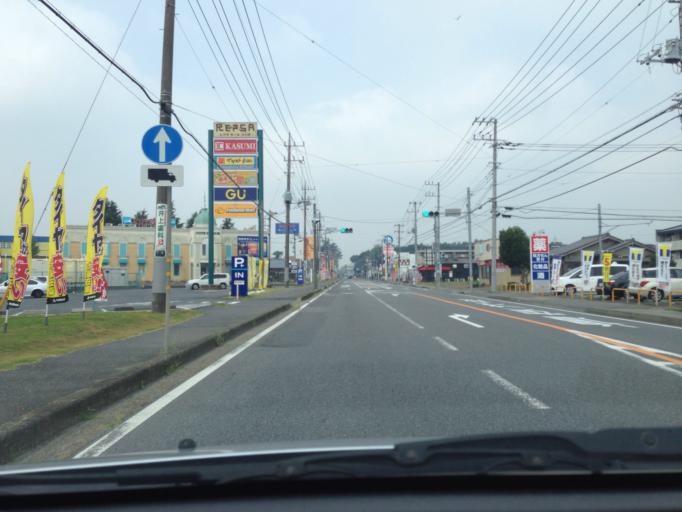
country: JP
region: Ibaraki
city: Naka
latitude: 36.0515
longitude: 140.1368
